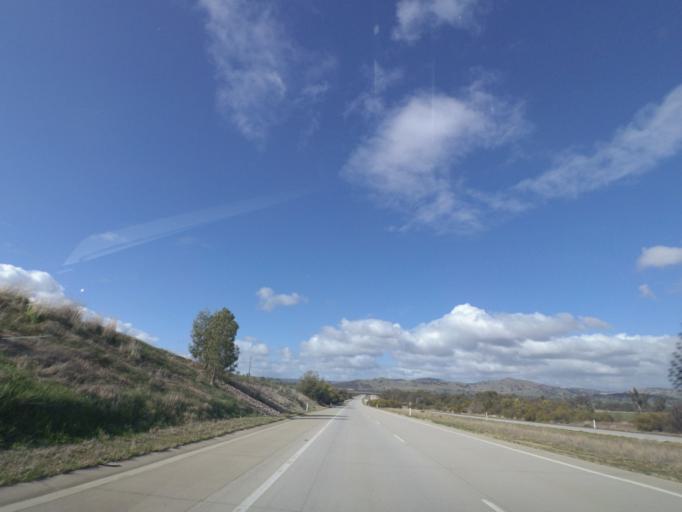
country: AU
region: New South Wales
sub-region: Albury Municipality
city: Lavington
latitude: -35.9154
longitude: 147.1195
